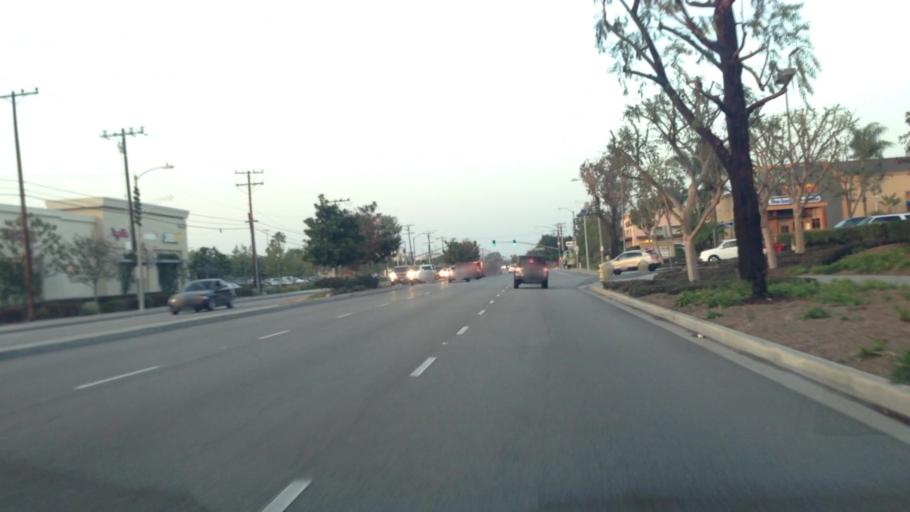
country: US
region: California
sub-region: Orange County
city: Rossmoor
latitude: 33.7824
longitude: -118.0719
